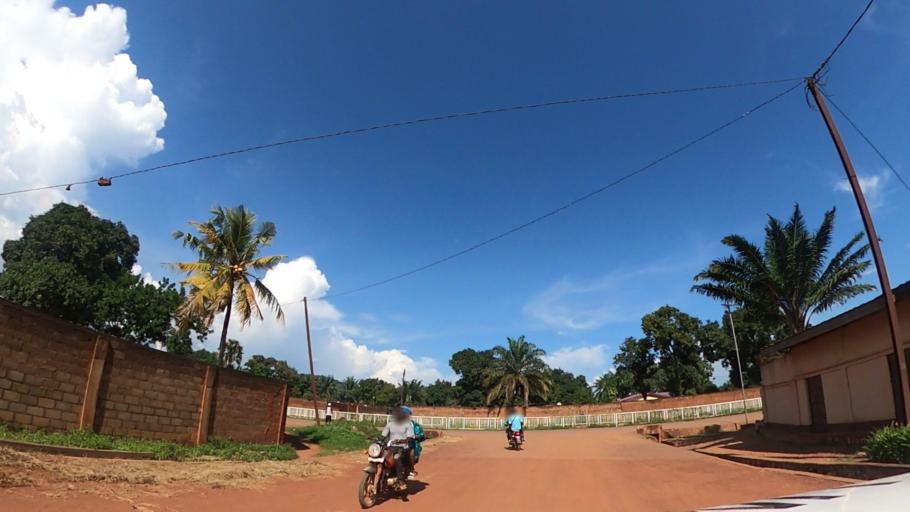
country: CF
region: Bangui
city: Bangui
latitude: 4.3740
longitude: 18.5512
